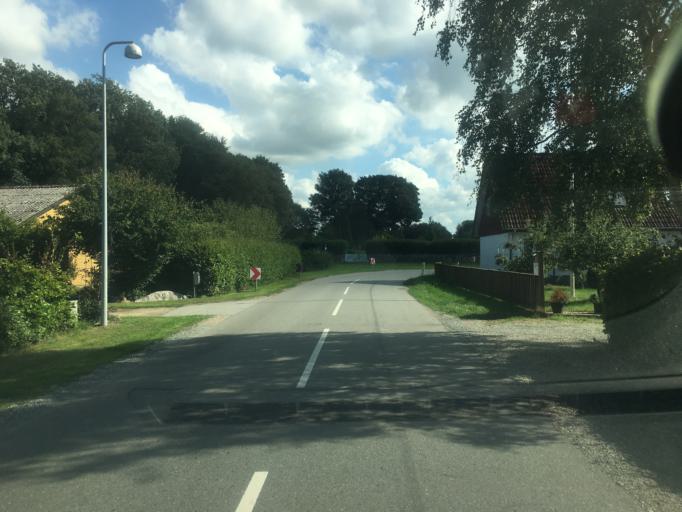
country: DE
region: Schleswig-Holstein
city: Ellhoft
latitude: 54.9488
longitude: 8.9654
